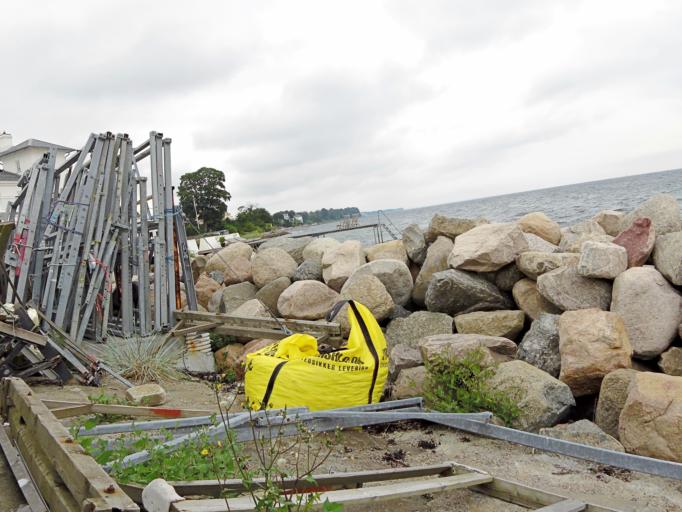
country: DK
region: Capital Region
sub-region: Gentofte Kommune
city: Charlottenlund
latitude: 55.7884
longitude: 12.5958
